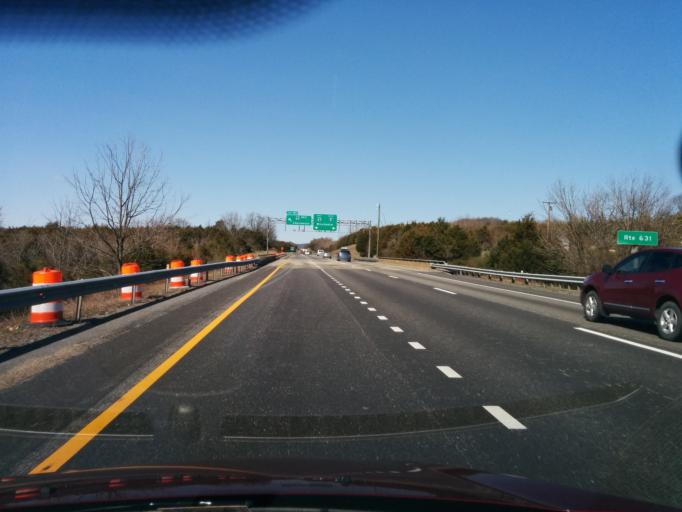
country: US
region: Virginia
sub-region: Rockbridge County
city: East Lexington
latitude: 37.7884
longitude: -79.3984
